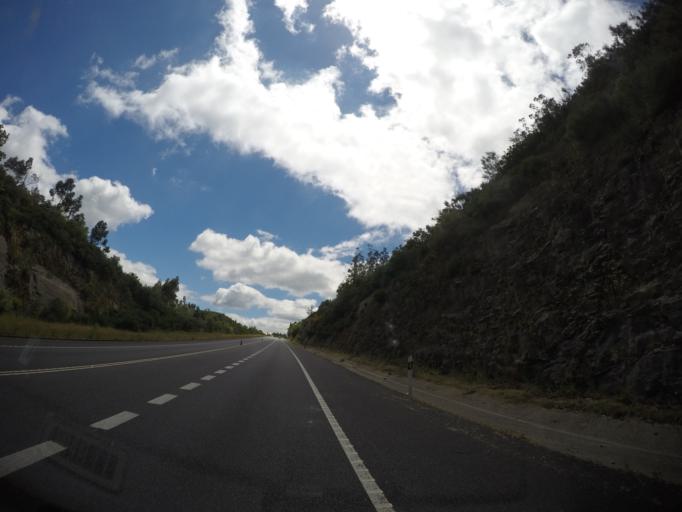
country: ES
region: Aragon
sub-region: Provincia de Zaragoza
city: El Burgo de Ebro
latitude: 41.5468
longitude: -0.7441
